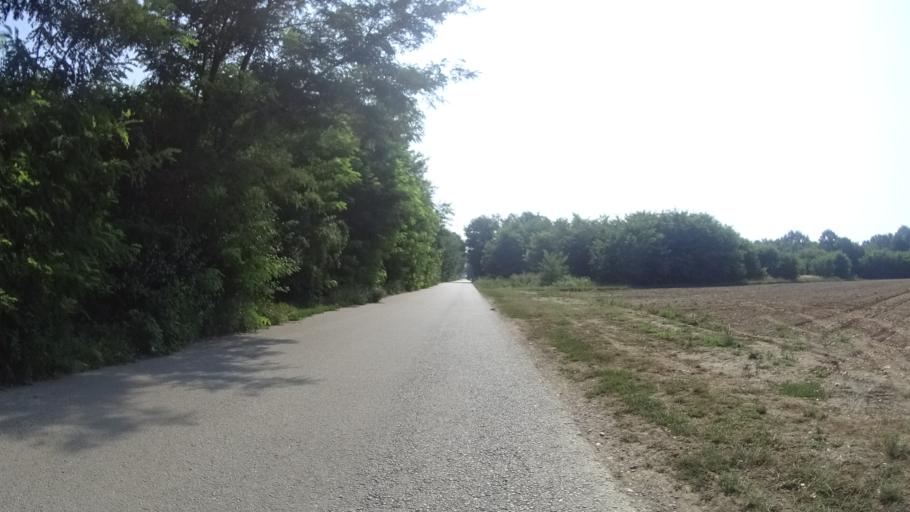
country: HR
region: Medimurska
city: Belica
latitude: 46.3959
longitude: 16.5156
